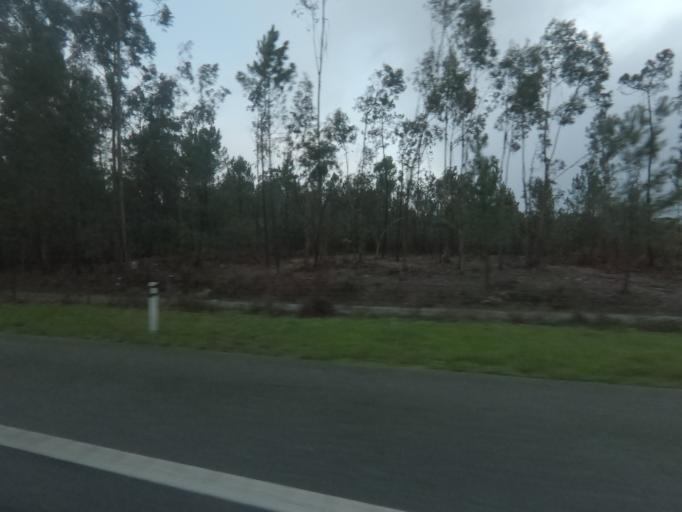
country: PT
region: Braga
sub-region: Barcelos
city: Galegos
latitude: 41.6231
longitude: -8.5565
